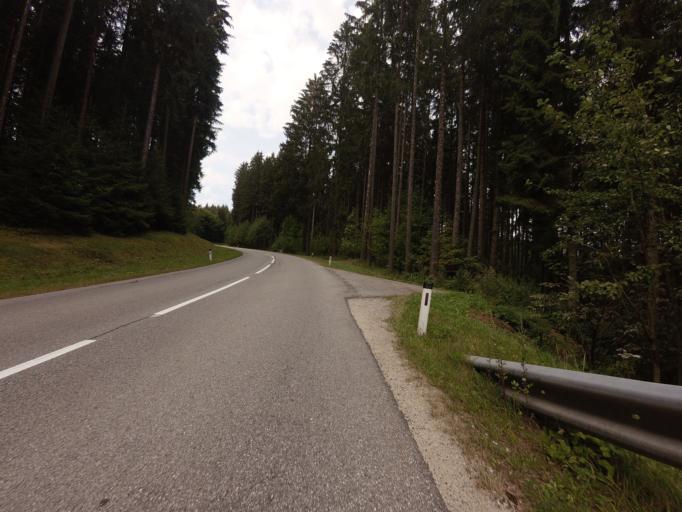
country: AT
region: Upper Austria
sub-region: Politischer Bezirk Urfahr-Umgebung
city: Reichenthal
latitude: 48.5542
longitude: 14.4053
